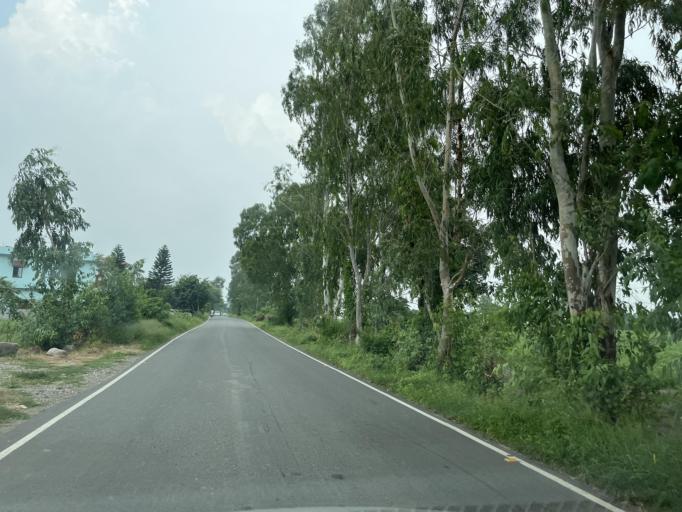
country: IN
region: Uttarakhand
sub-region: Naini Tal
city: Haldwani
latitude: 29.1758
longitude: 79.4706
